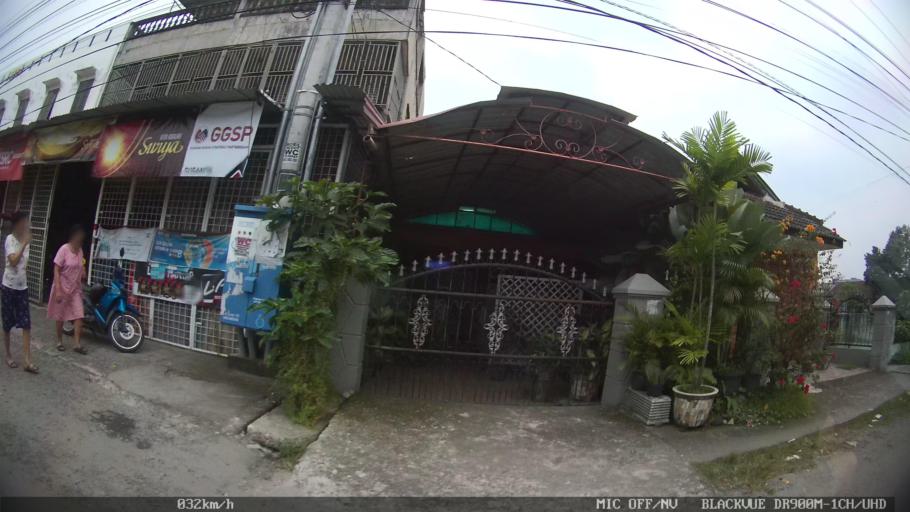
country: ID
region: North Sumatra
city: Medan
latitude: 3.5628
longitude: 98.7002
